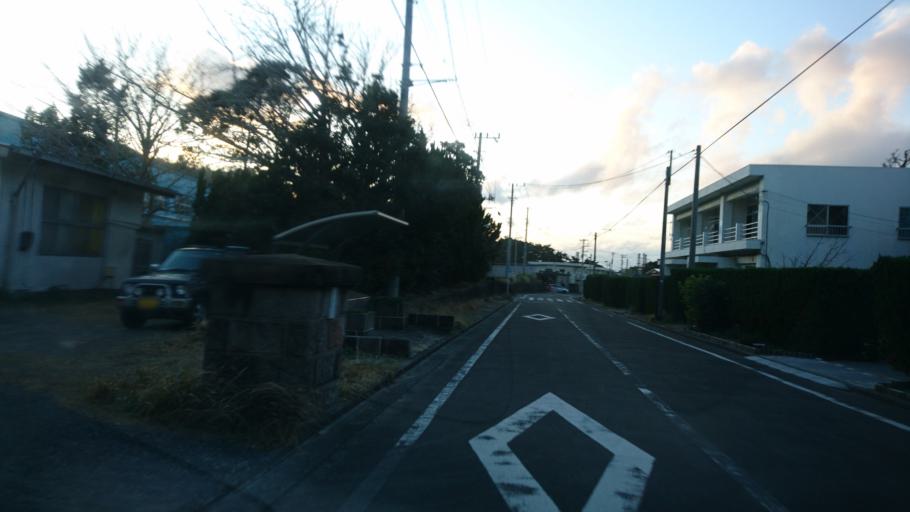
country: JP
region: Shizuoka
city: Shimoda
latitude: 34.3720
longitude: 139.2586
